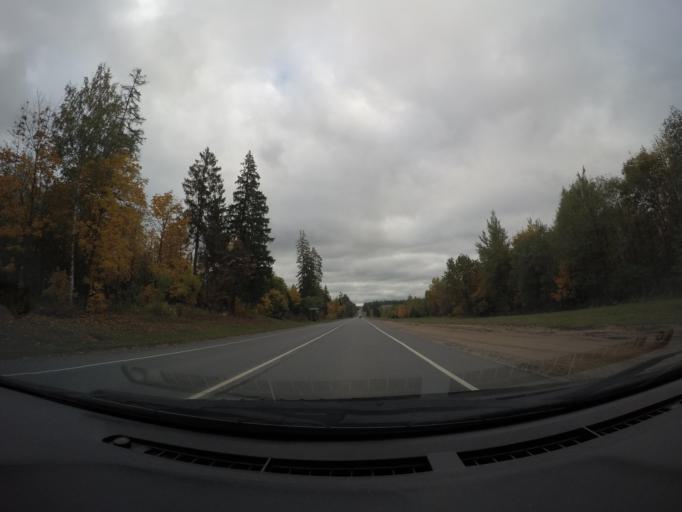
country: RU
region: Moskovskaya
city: Dorokhovo
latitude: 55.6209
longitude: 36.3441
